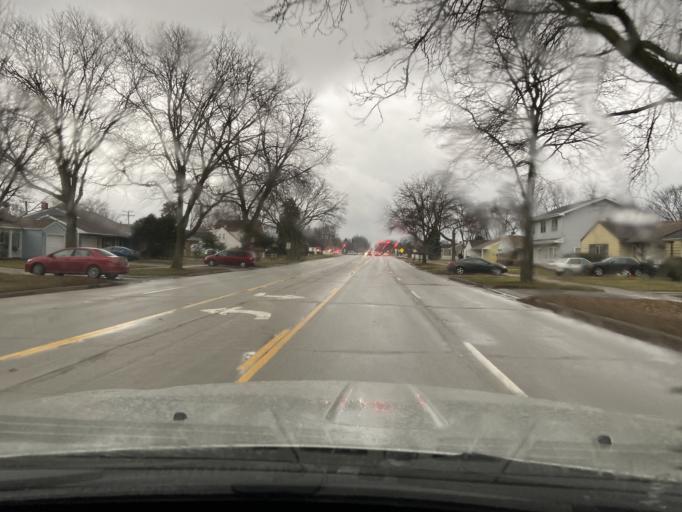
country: US
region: Illinois
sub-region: Cook County
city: Des Plaines
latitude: 42.0328
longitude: -87.9091
